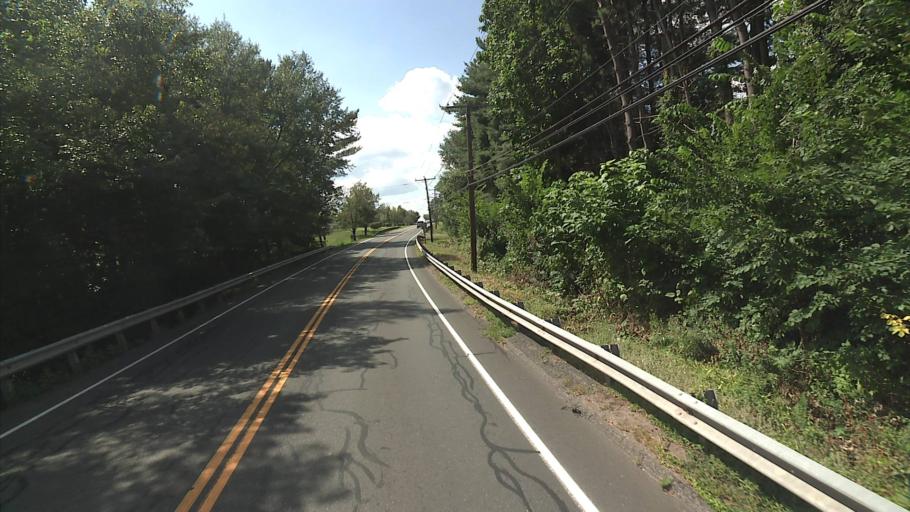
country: US
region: Connecticut
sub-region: Tolland County
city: Somers
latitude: 41.9839
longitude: -72.4560
